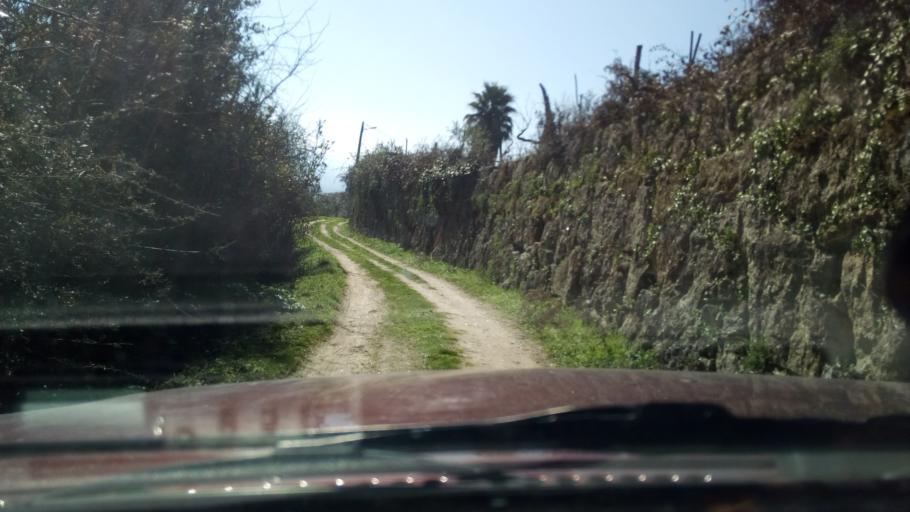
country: PT
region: Guarda
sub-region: Fornos de Algodres
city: Fornos de Algodres
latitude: 40.6254
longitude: -7.5372
